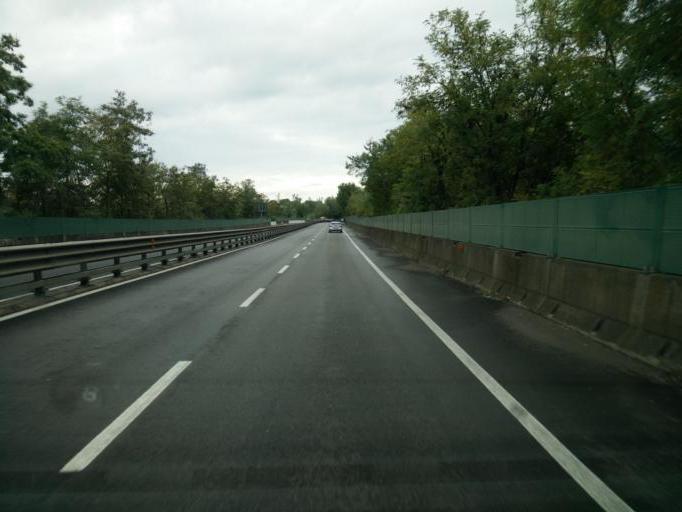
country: IT
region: Tuscany
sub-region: Provincia di Siena
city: Poggibonsi
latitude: 43.4726
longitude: 11.1532
